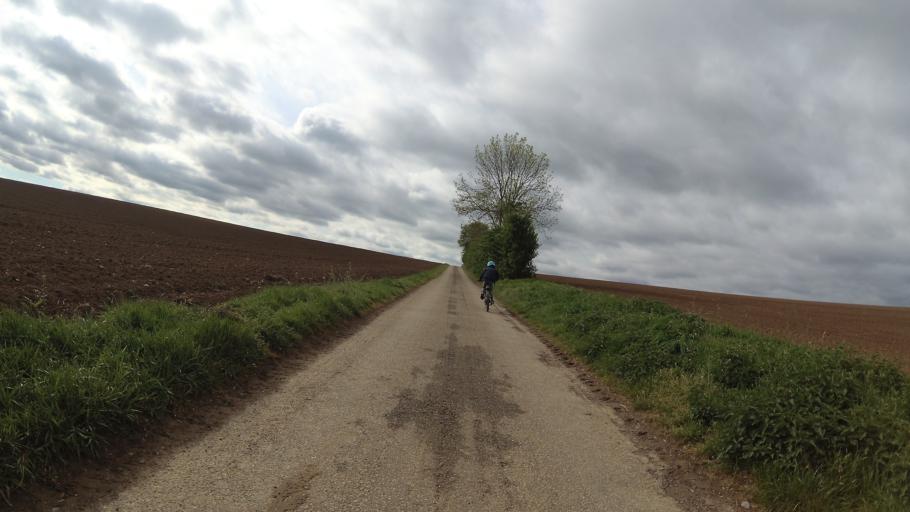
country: DE
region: Baden-Wuerttemberg
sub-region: Regierungsbezirk Stuttgart
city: Oedheim
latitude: 49.2183
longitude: 9.2609
